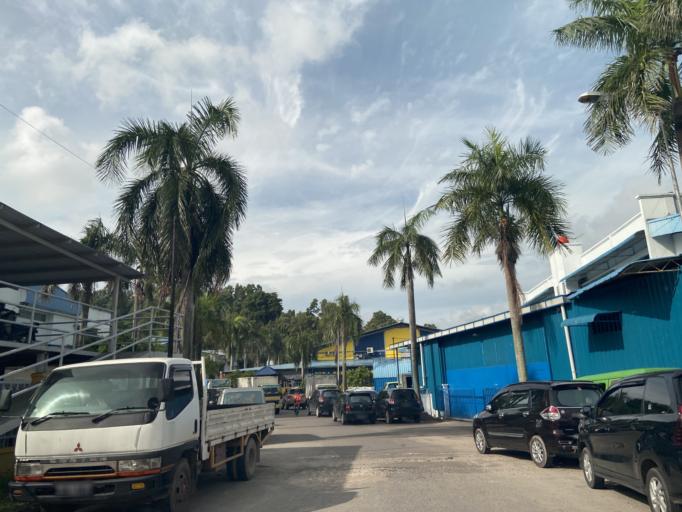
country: SG
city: Singapore
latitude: 1.1489
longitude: 104.0201
